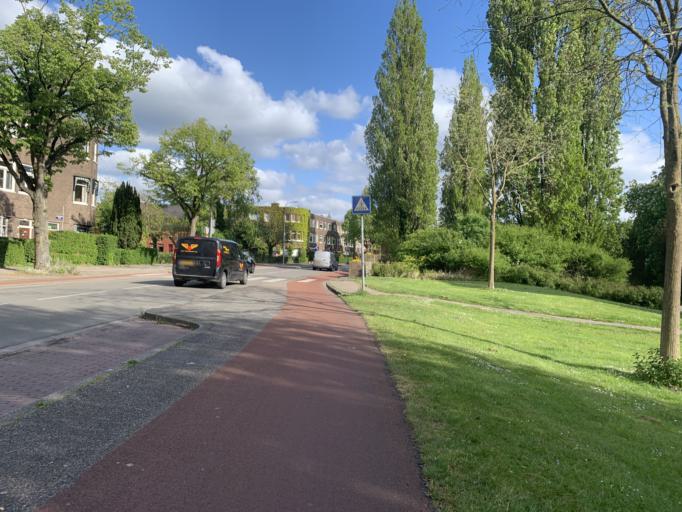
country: NL
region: Groningen
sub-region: Gemeente Groningen
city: Oosterpark
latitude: 53.2242
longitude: 6.5765
